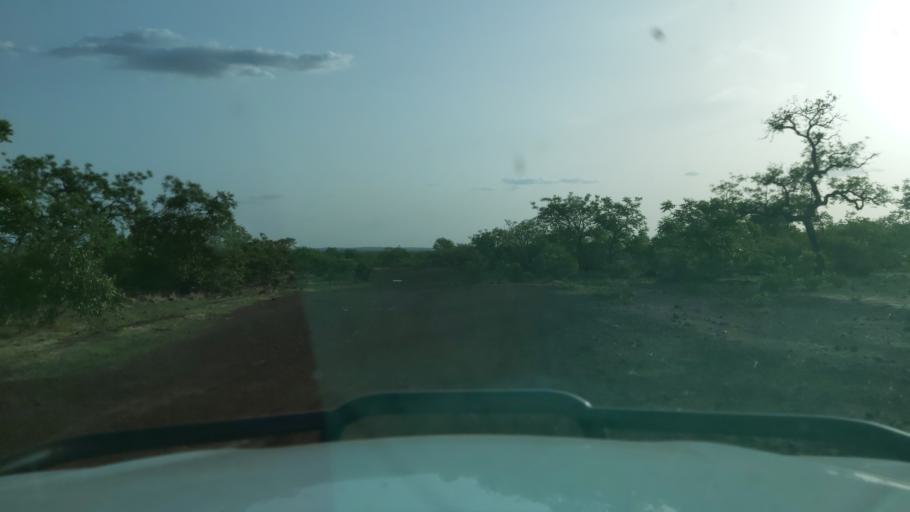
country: ML
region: Koulikoro
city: Kolokani
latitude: 13.2102
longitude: -7.9044
